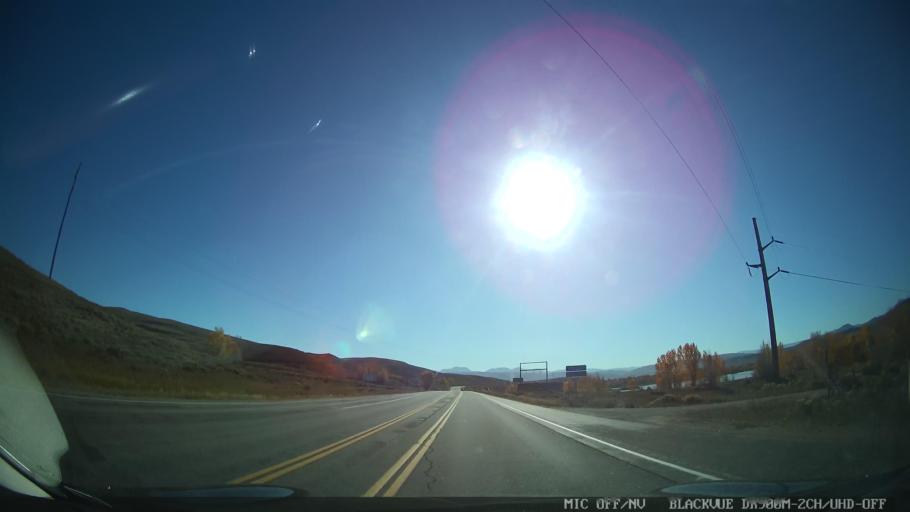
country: US
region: Colorado
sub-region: Grand County
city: Granby
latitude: 40.1098
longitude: -105.9856
